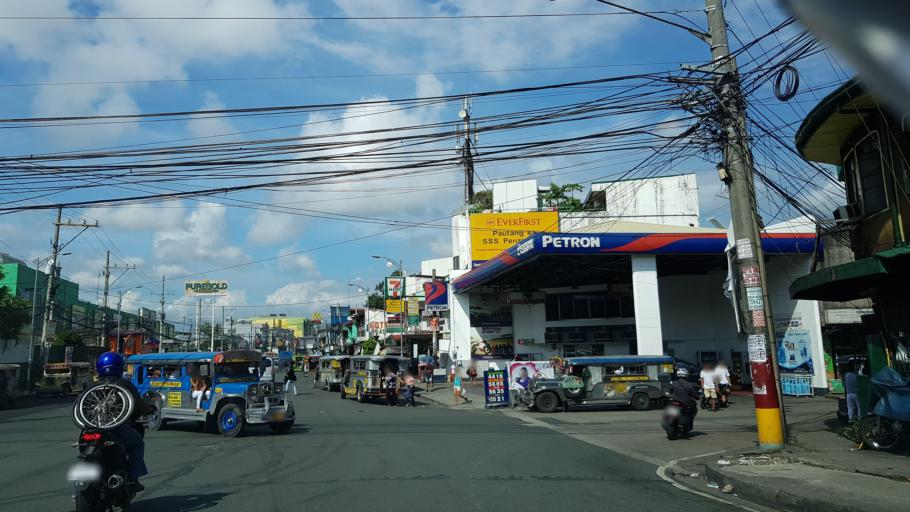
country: PH
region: Metro Manila
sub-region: San Juan
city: San Juan
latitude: 14.5872
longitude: 121.0207
